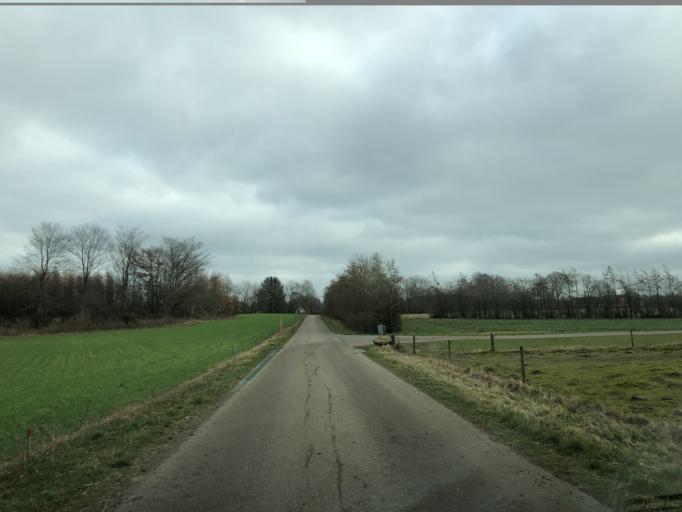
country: DK
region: South Denmark
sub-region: Billund Kommune
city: Billund
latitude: 55.7834
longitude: 9.1562
